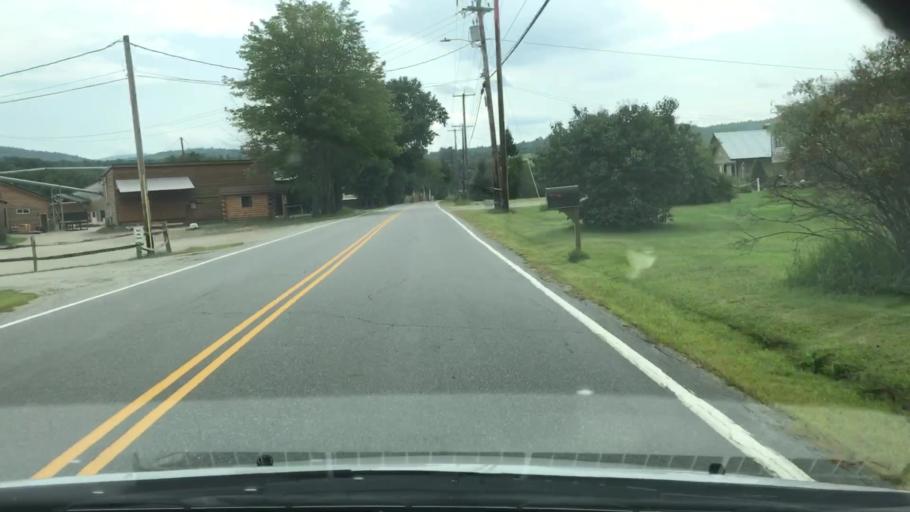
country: US
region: New Hampshire
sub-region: Grafton County
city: Woodsville
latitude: 44.1420
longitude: -72.0358
